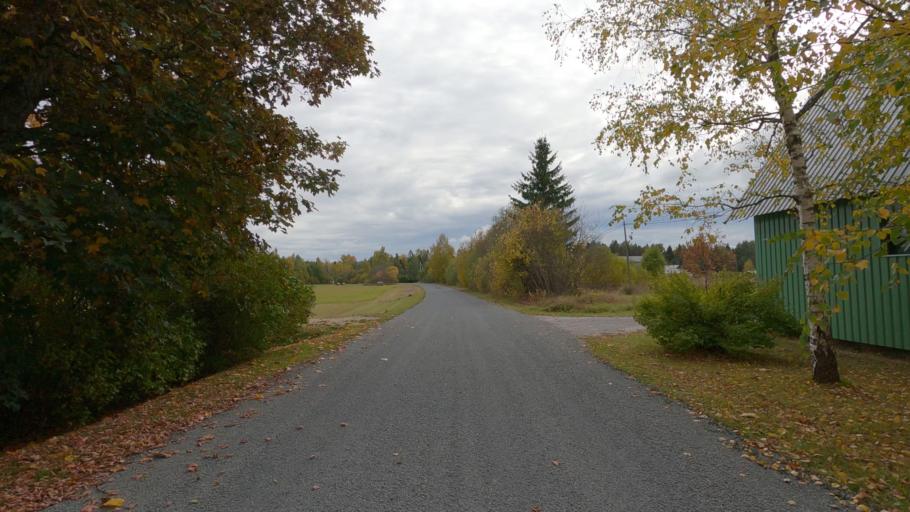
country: EE
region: Raplamaa
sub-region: Rapla vald
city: Rapla
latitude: 58.9881
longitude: 24.7801
